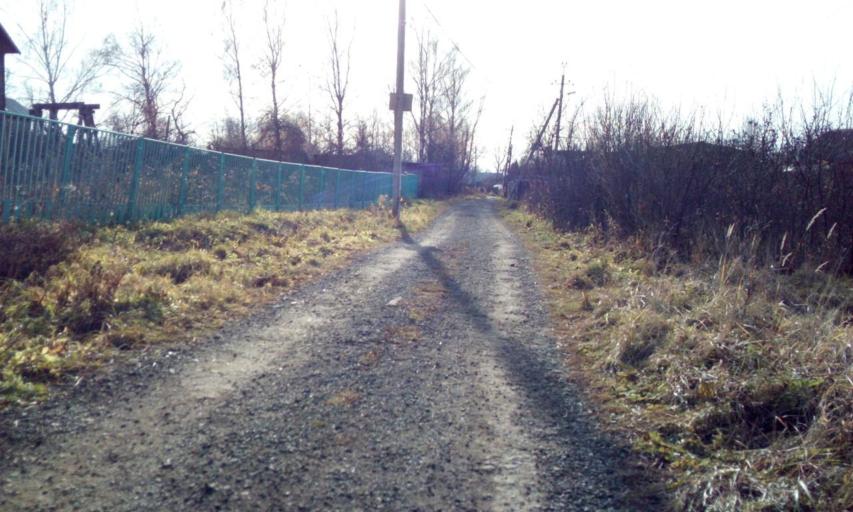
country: RU
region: Moskovskaya
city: Zhavoronki
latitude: 55.6550
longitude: 37.1523
